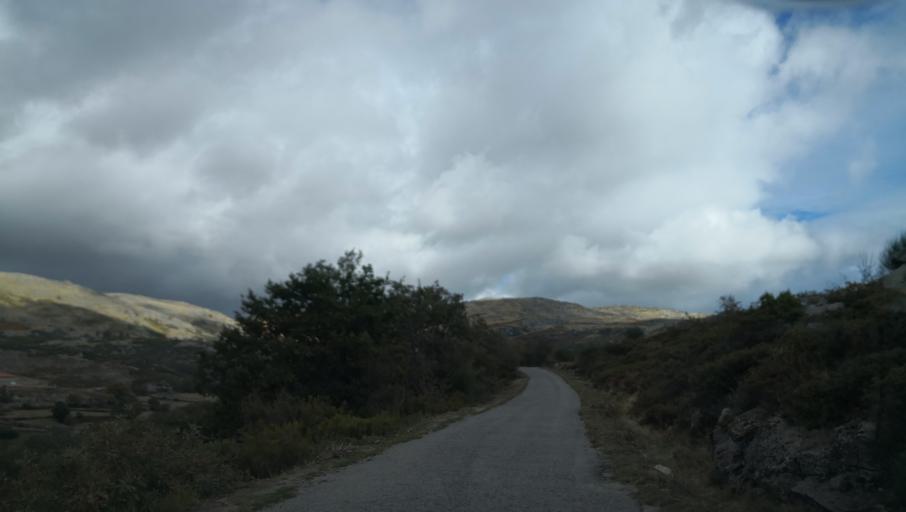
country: PT
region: Vila Real
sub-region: Vila Real
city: Vila Real
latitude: 41.3819
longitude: -7.8090
